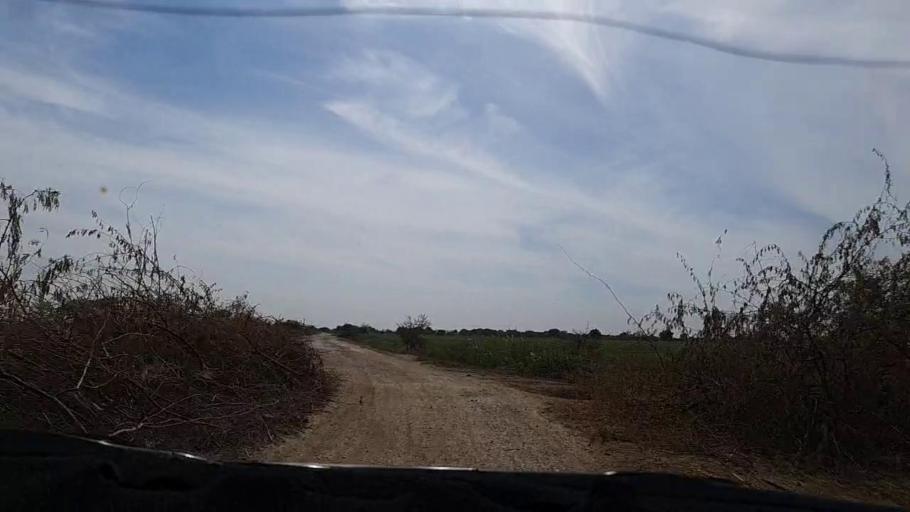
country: PK
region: Sindh
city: Pithoro
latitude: 25.4752
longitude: 69.4576
